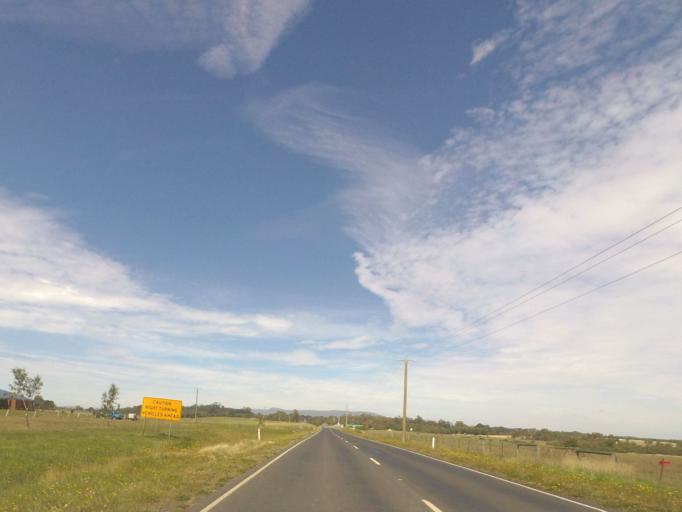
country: AU
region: Victoria
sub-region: Mount Alexander
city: Castlemaine
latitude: -37.2872
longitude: 144.5020
